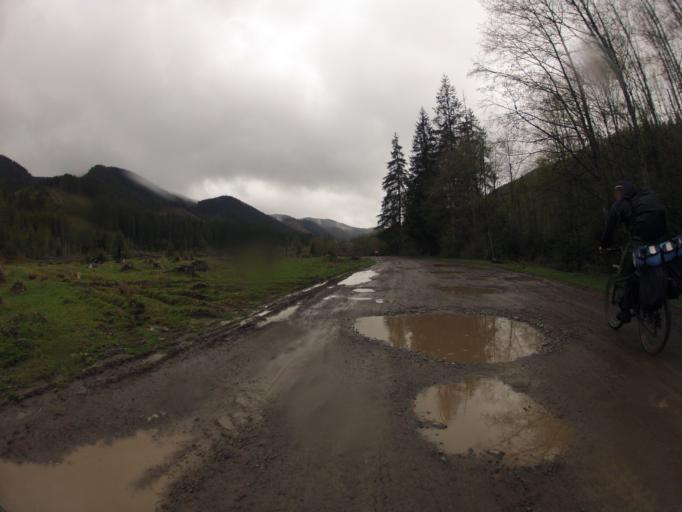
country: RO
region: Suceava
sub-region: Comuna Izvoarele Sucevei
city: Izvoarele Sucevei
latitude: 47.8336
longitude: 25.0556
